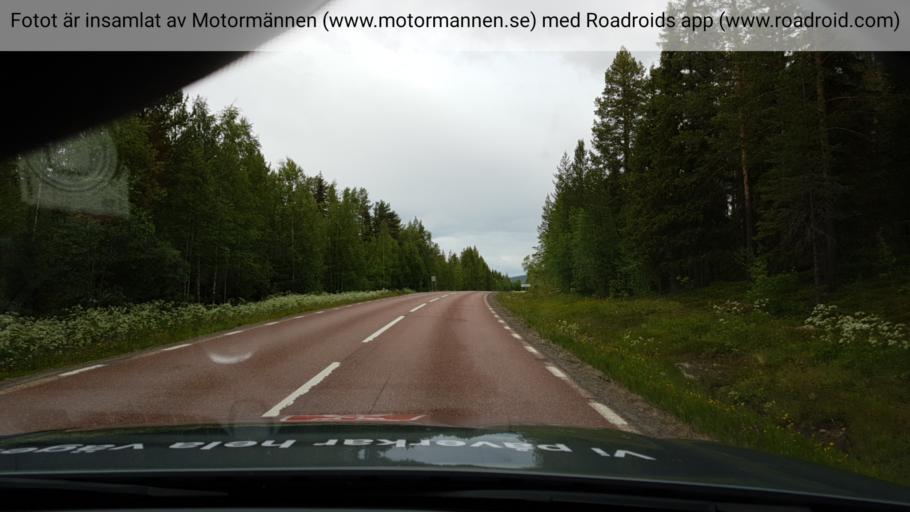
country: SE
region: Vaesterbotten
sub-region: Dorotea Kommun
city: Dorotea
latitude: 64.0928
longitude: 16.0870
